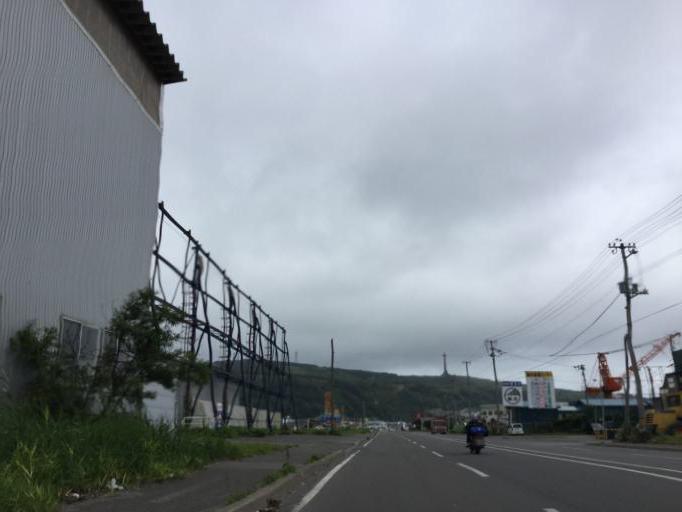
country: JP
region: Hokkaido
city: Wakkanai
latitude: 45.4034
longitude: 141.6840
